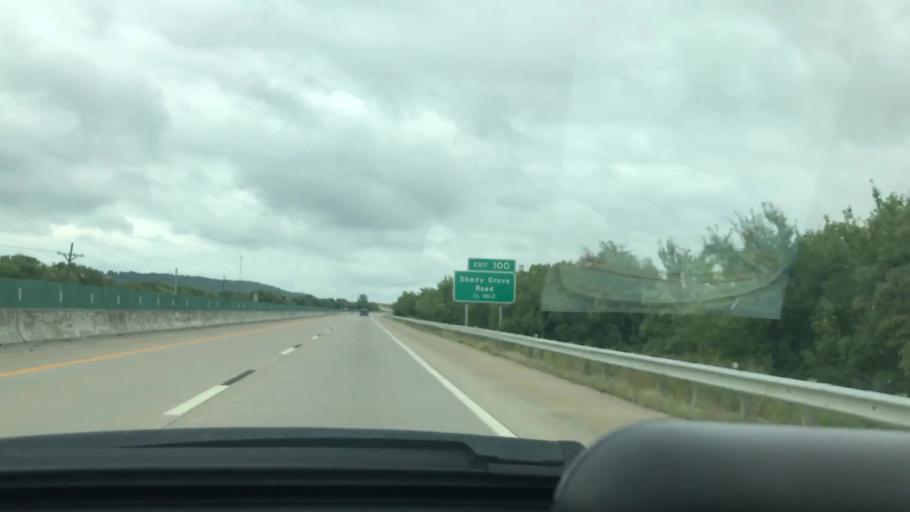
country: US
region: Oklahoma
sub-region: Pittsburg County
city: Krebs
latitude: 35.0470
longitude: -95.7100
